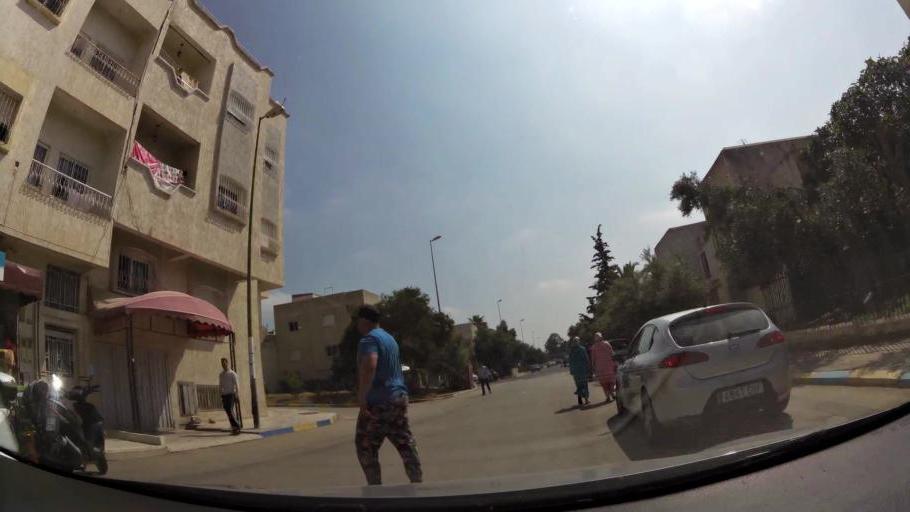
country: MA
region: Fes-Boulemane
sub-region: Fes
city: Fes
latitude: 34.0579
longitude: -5.0237
